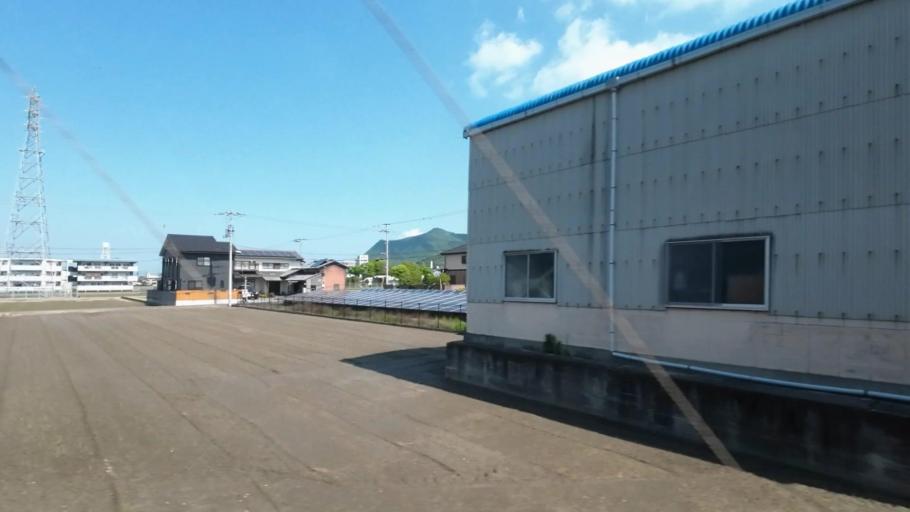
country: JP
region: Kagawa
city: Kan'onjicho
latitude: 34.1289
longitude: 133.6704
